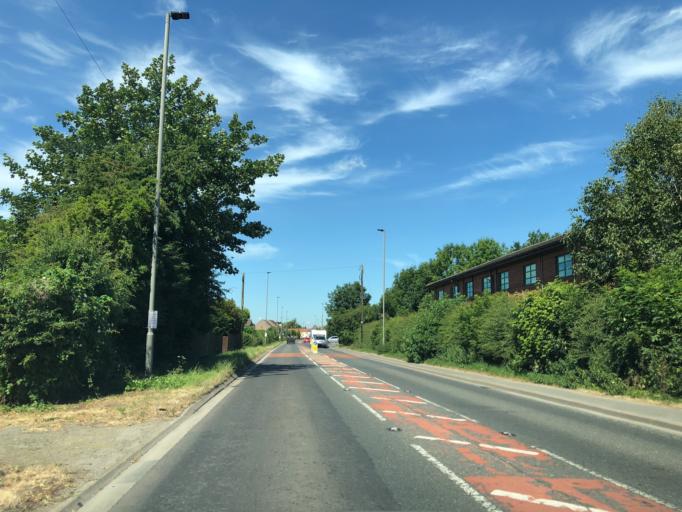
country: GB
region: England
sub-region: North Yorkshire
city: Thirsk
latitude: 54.2310
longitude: -1.3323
